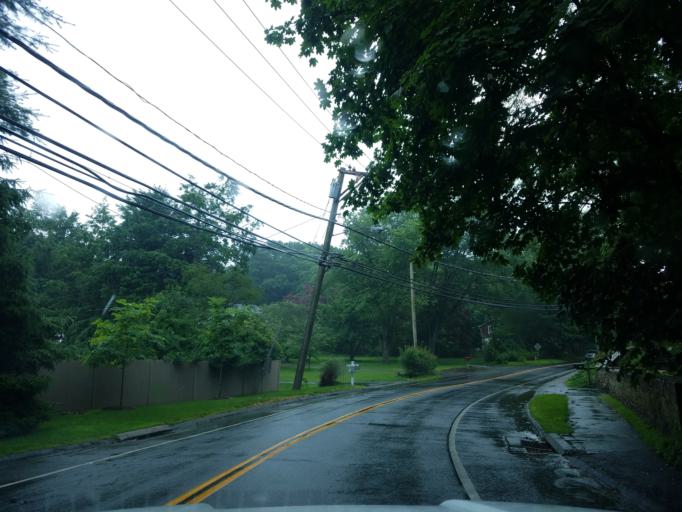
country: US
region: Connecticut
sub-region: Fairfield County
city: Westport
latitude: 41.1451
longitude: -73.3682
